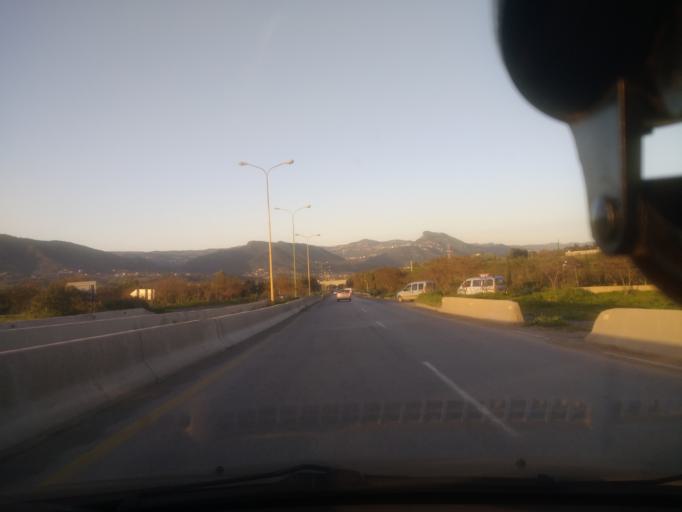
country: DZ
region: Boumerdes
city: Draa Ben Khedda
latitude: 36.7406
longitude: 4.0078
